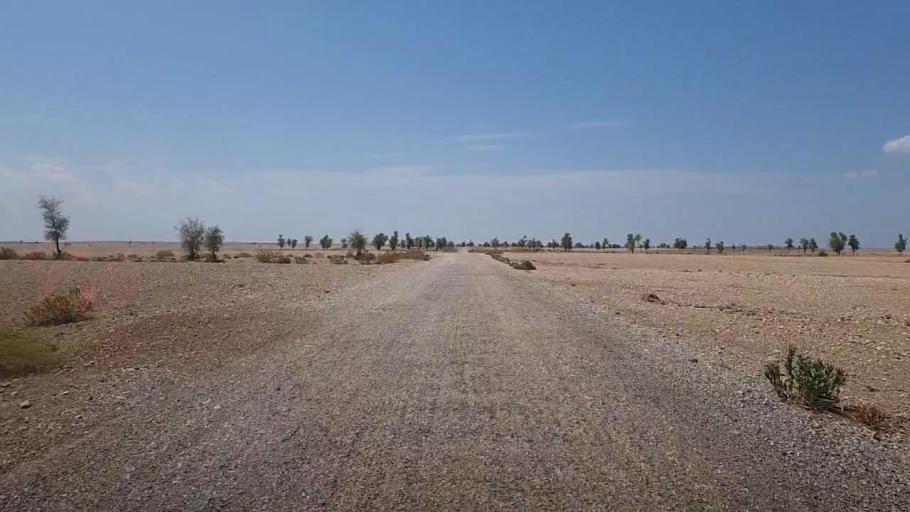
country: PK
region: Sindh
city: Sehwan
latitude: 26.3322
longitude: 67.6784
